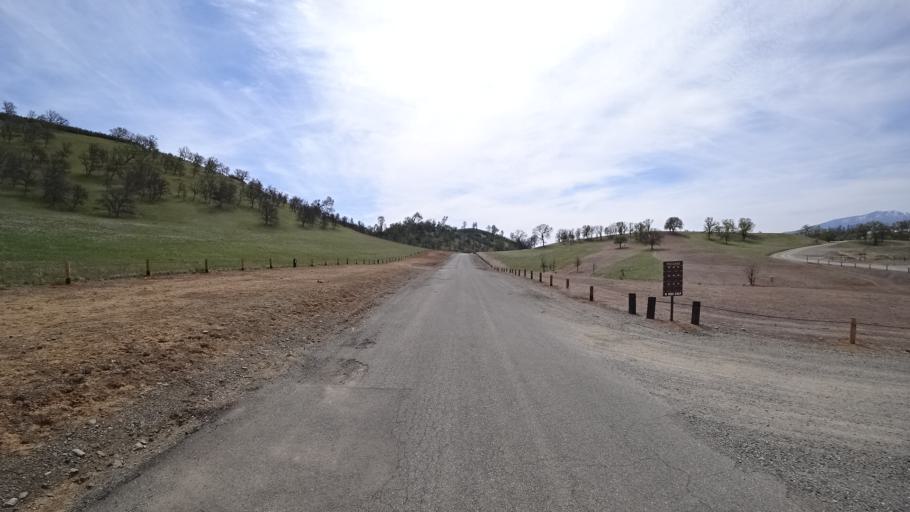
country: US
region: California
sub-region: Glenn County
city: Willows
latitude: 39.5925
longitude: -122.5240
